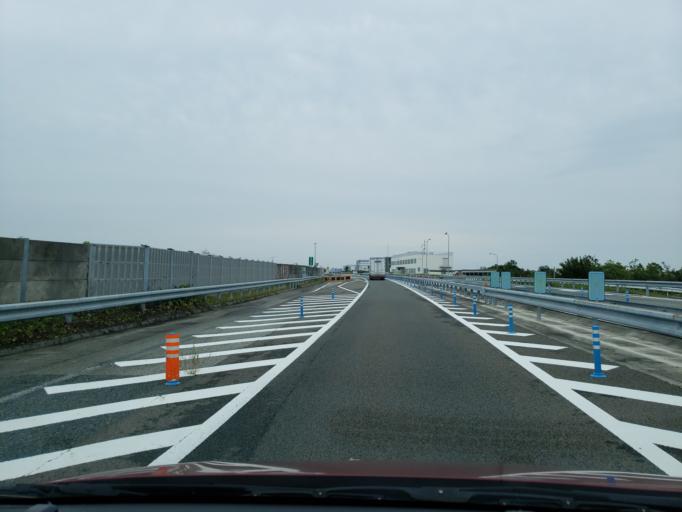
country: JP
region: Tokushima
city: Tokushima-shi
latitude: 34.1064
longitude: 134.5392
